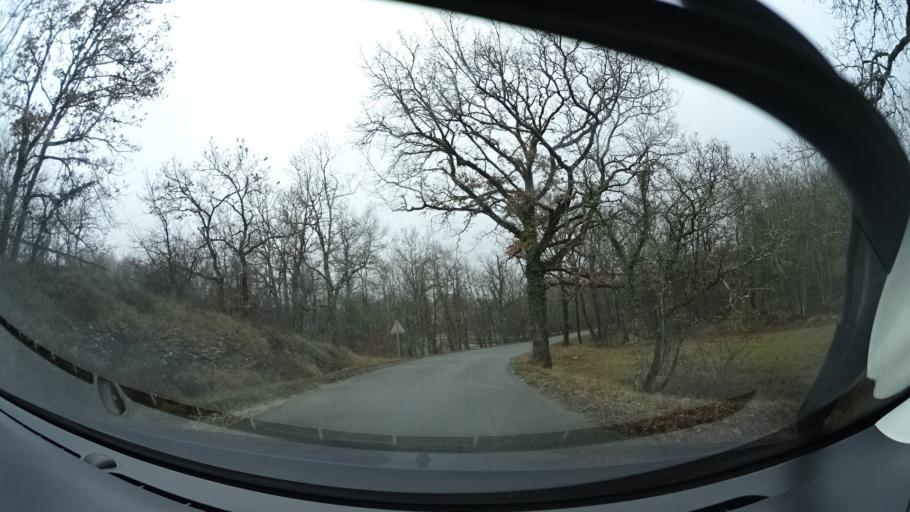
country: FR
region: Midi-Pyrenees
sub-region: Departement du Lot
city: Montcuq
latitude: 44.3844
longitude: 1.2245
